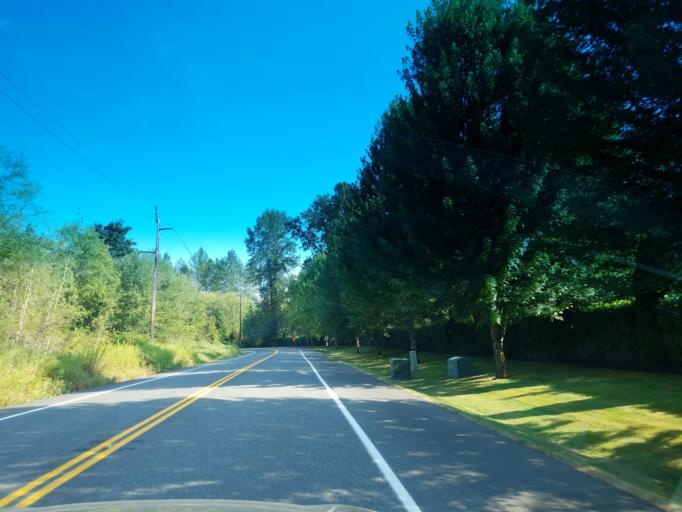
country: US
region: Washington
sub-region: King County
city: Union Hill-Novelty Hill
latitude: 47.6583
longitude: -122.0029
